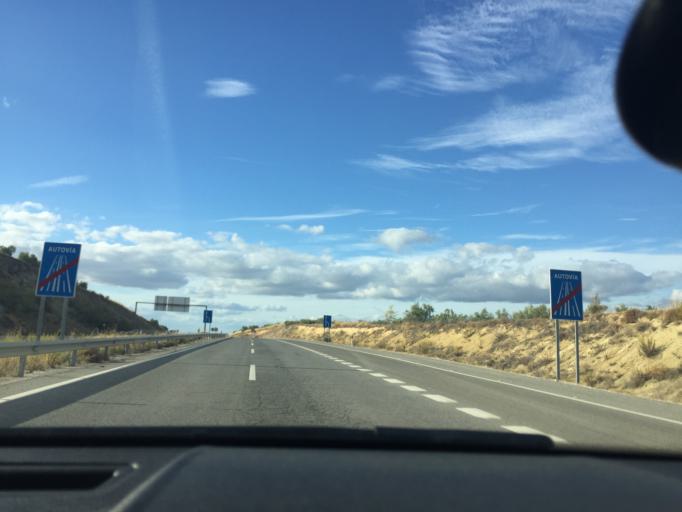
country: ES
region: Andalusia
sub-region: Provincia de Jaen
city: Torredonjimeno
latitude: 37.7541
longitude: -3.9589
